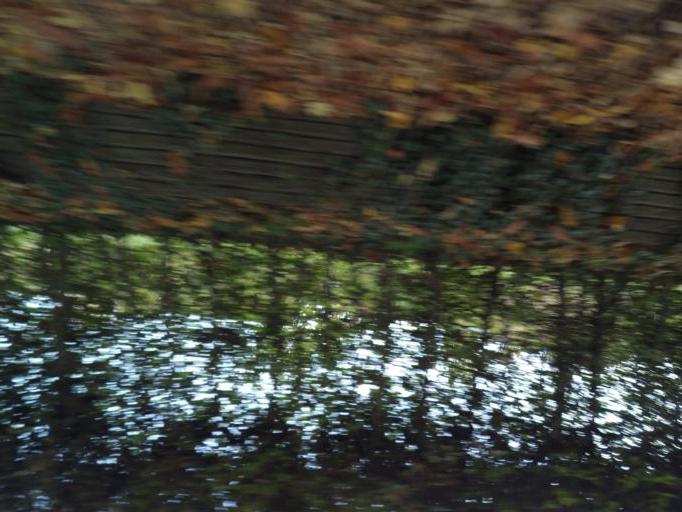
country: DK
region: Central Jutland
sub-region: Arhus Kommune
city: Stavtrup
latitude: 56.1584
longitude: 10.1125
